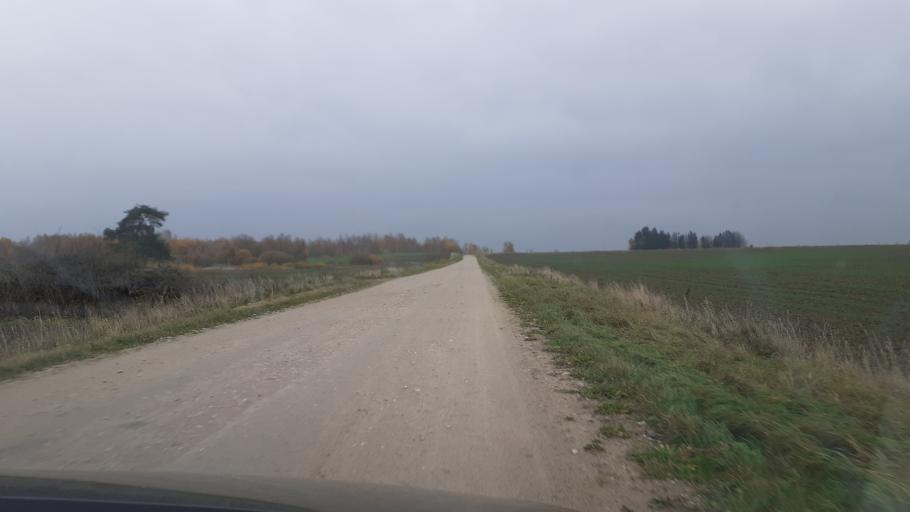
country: LV
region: Saldus Rajons
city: Saldus
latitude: 56.8649
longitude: 22.2869
